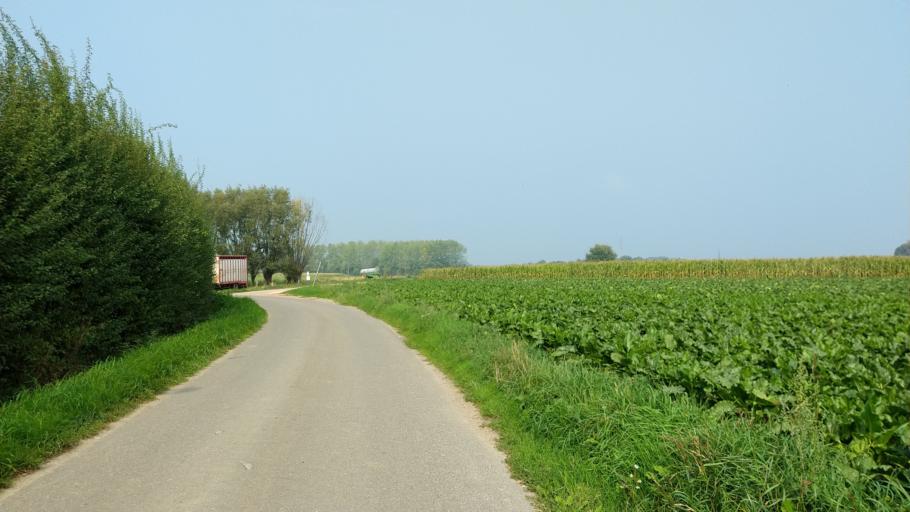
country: BE
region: Flanders
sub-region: Provincie Vlaams-Brabant
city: Haacht
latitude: 50.9497
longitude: 4.6652
